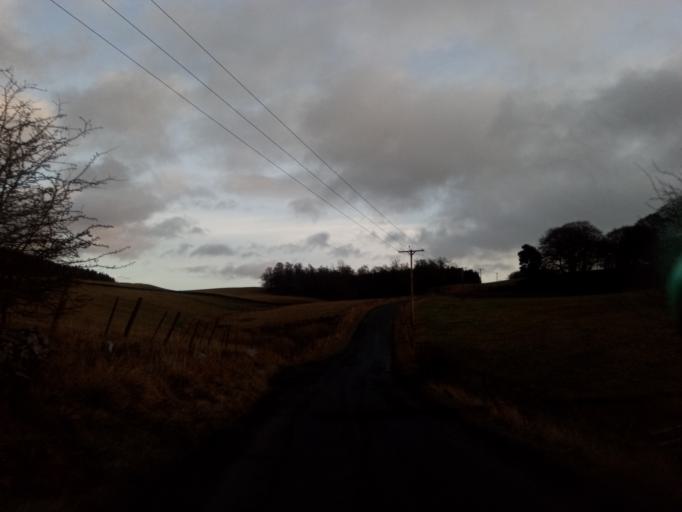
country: GB
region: Scotland
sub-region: The Scottish Borders
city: Selkirk
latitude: 55.5612
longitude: -2.7938
